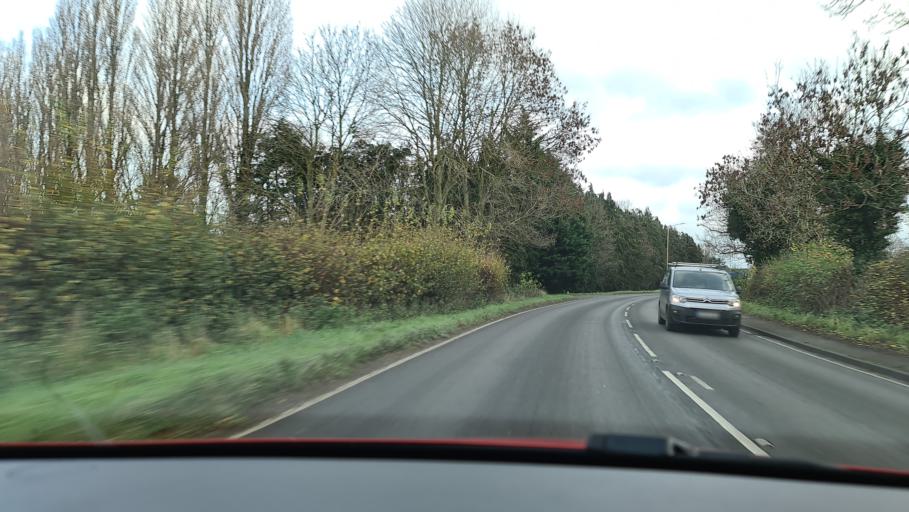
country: GB
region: England
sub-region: Buckinghamshire
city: Weston Turville
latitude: 51.7648
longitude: -0.7873
